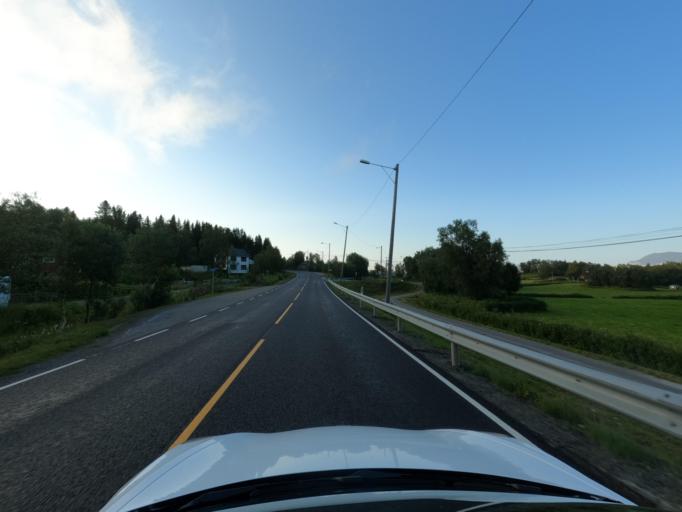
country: NO
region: Troms
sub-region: Skanland
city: Evenskjer
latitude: 68.6678
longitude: 16.5759
